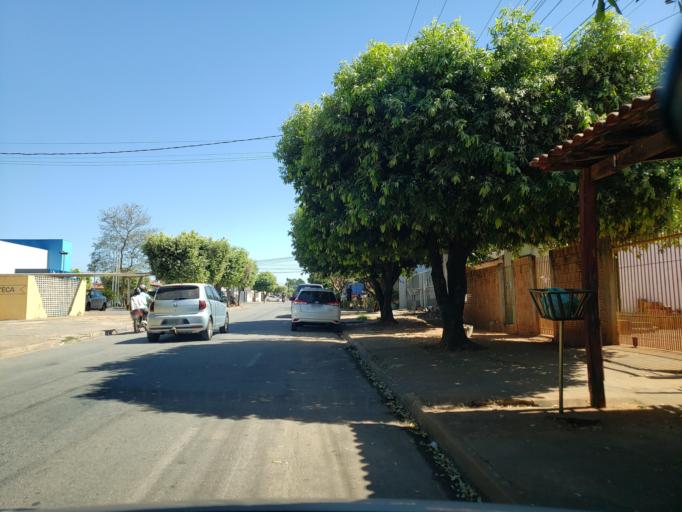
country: BR
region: Mato Grosso
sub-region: Rondonopolis
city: Rondonopolis
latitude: -16.4417
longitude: -54.6247
